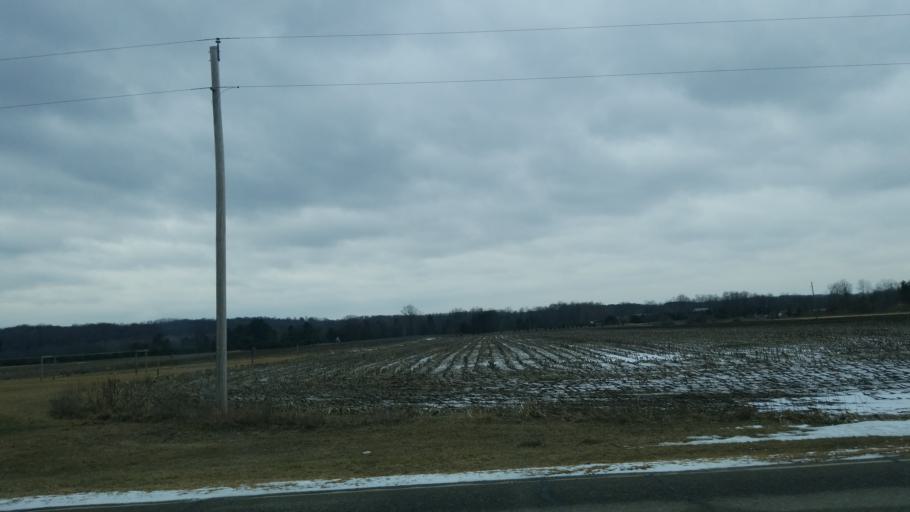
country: US
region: Michigan
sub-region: Osceola County
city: Reed City
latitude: 43.8284
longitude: -85.4241
